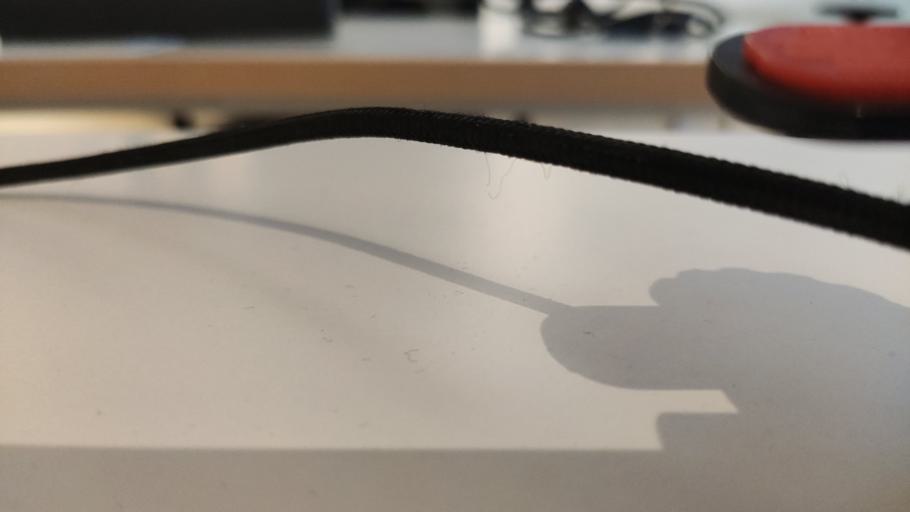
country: RU
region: Moskovskaya
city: Ruza
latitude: 55.7890
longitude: 36.2809
